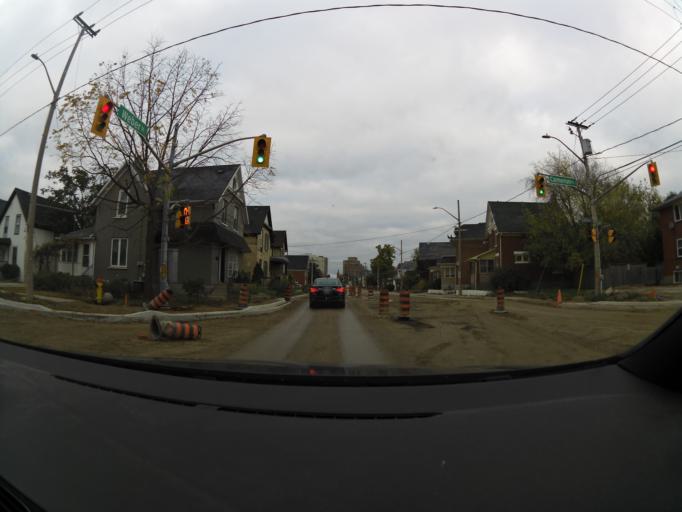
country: CA
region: Ontario
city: Kitchener
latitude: 43.4481
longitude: -80.4790
